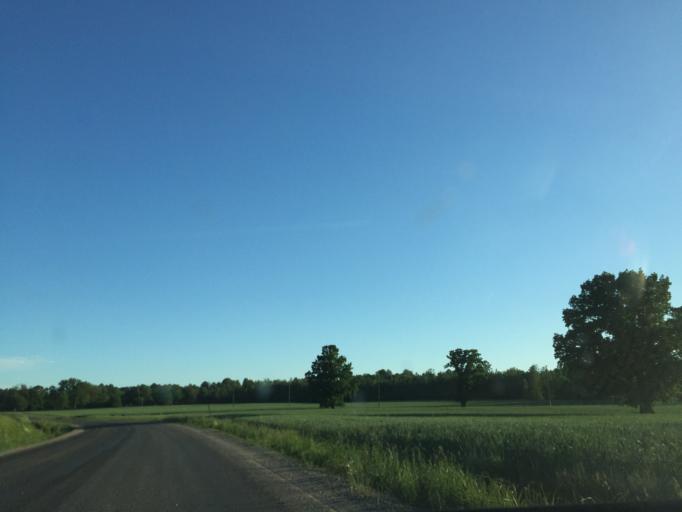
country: LV
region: Broceni
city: Broceni
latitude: 56.7395
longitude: 22.5100
